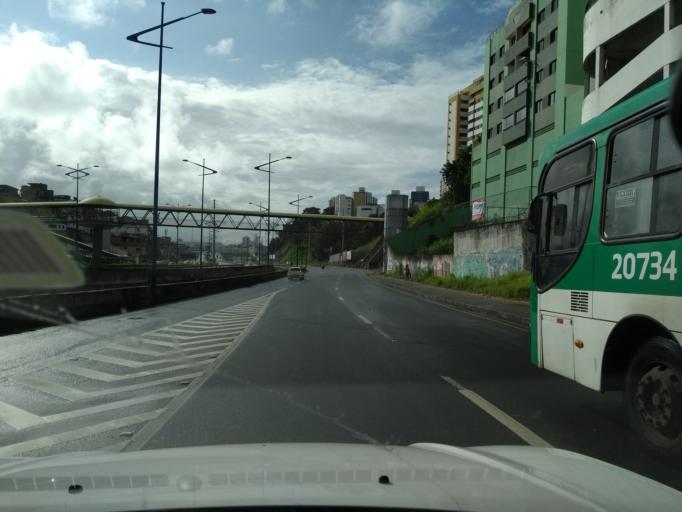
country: BR
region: Bahia
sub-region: Salvador
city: Salvador
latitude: -12.9676
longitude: -38.4896
